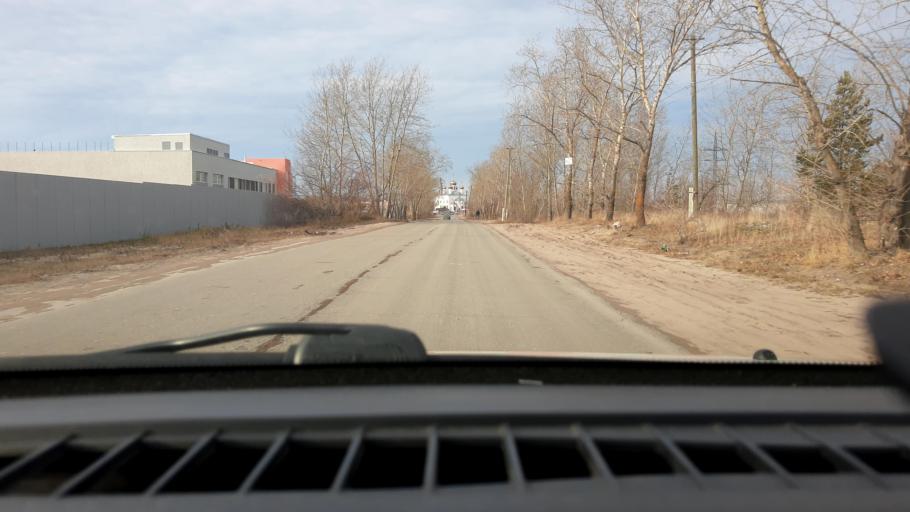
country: RU
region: Nizjnij Novgorod
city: Gorbatovka
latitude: 56.3580
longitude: 43.7981
